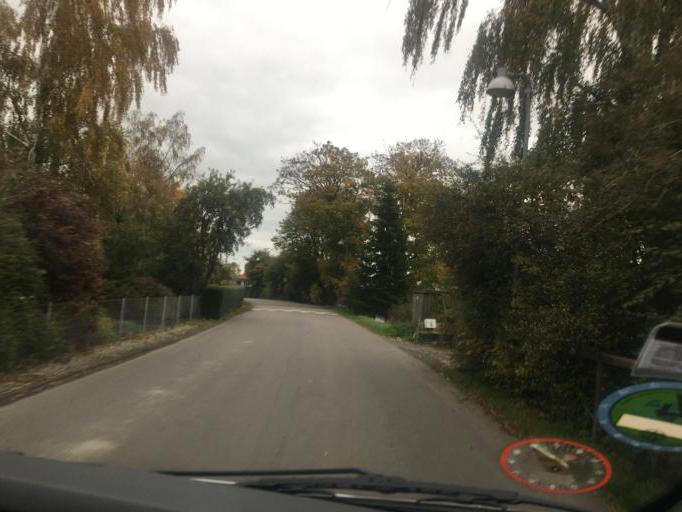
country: DK
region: Zealand
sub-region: Koge Kommune
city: Bjaeverskov
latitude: 55.4256
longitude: 11.9844
